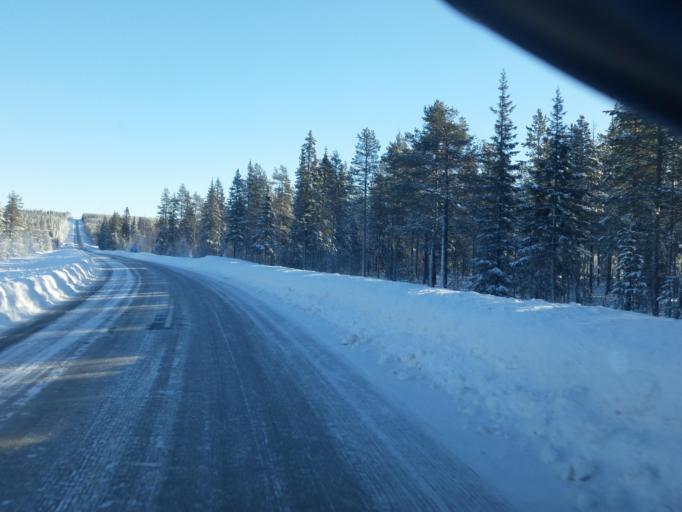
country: SE
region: Vaesterbotten
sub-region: Skelleftea Kommun
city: Storvik
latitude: 65.3250
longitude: 20.6965
